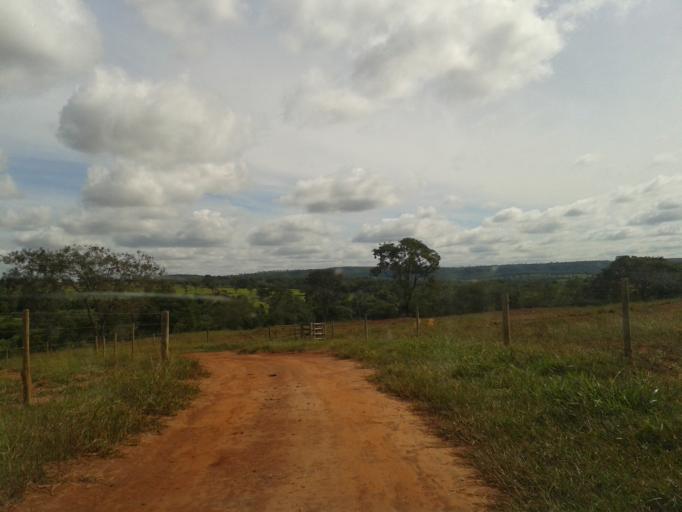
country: BR
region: Minas Gerais
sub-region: Campina Verde
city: Campina Verde
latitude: -19.4266
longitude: -49.7102
